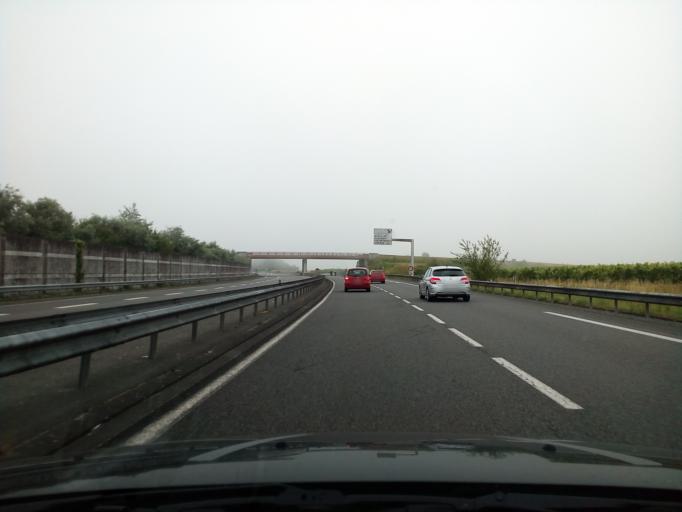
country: FR
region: Poitou-Charentes
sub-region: Departement de la Charente
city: Jarnac
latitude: 45.6942
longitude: -0.1351
